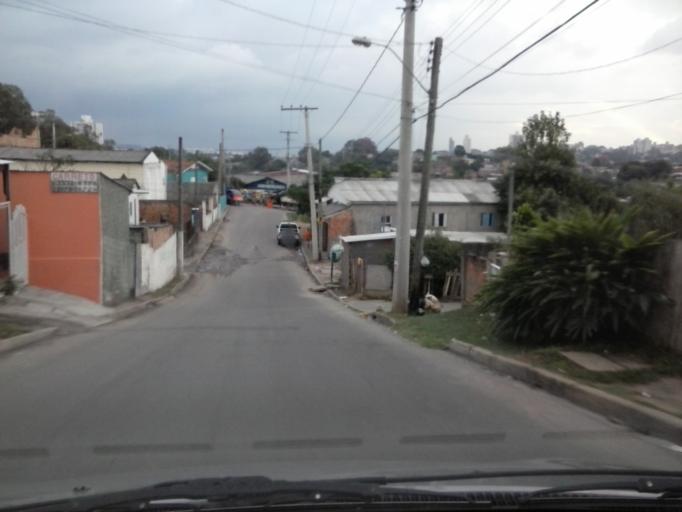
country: BR
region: Rio Grande do Sul
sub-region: Porto Alegre
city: Porto Alegre
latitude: -30.0504
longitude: -51.1558
